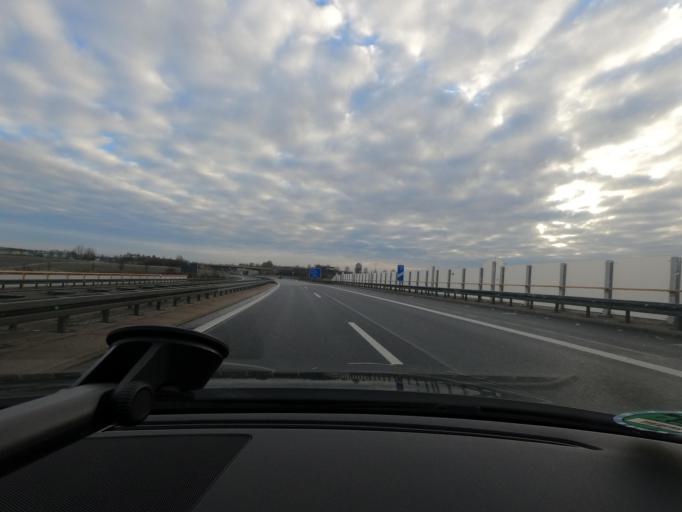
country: DE
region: Bavaria
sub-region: Upper Franconia
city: Coburg
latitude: 50.2913
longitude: 10.9723
